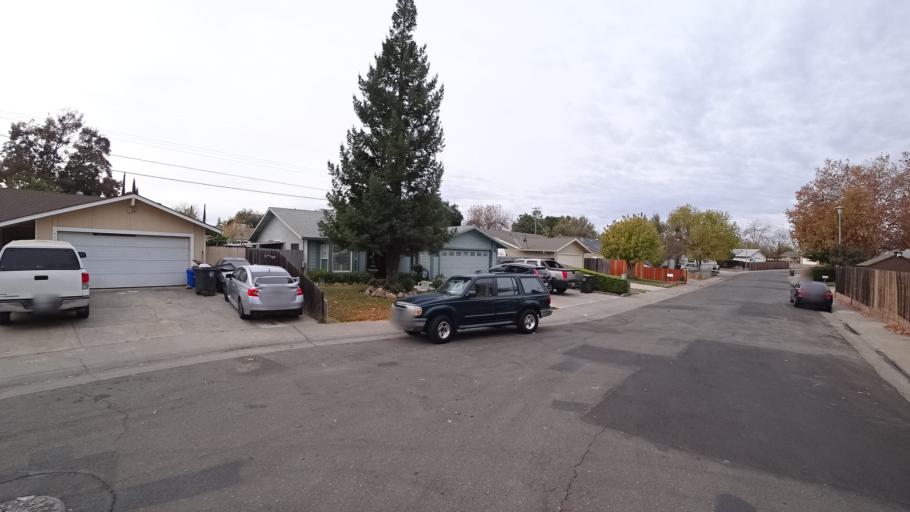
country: US
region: California
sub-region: Sacramento County
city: Citrus Heights
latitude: 38.7150
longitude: -121.2959
